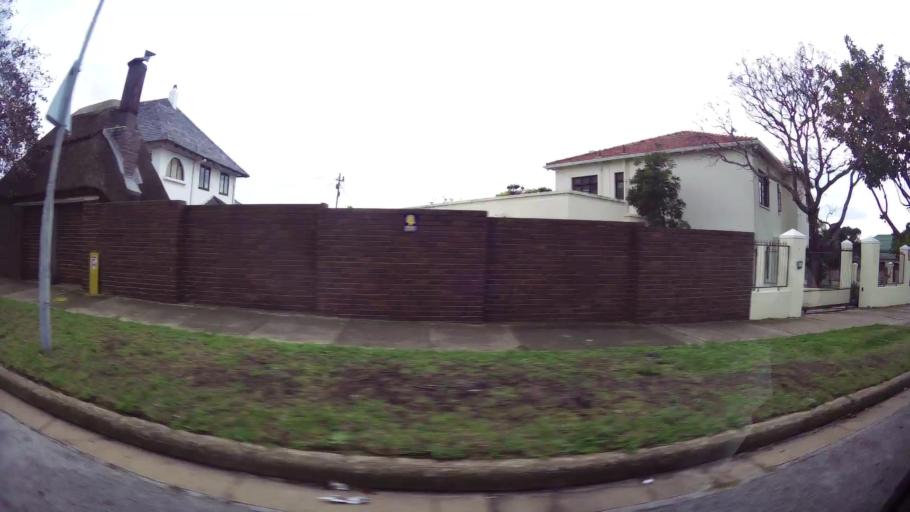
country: ZA
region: Eastern Cape
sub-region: Nelson Mandela Bay Metropolitan Municipality
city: Port Elizabeth
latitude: -33.9560
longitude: 25.5988
